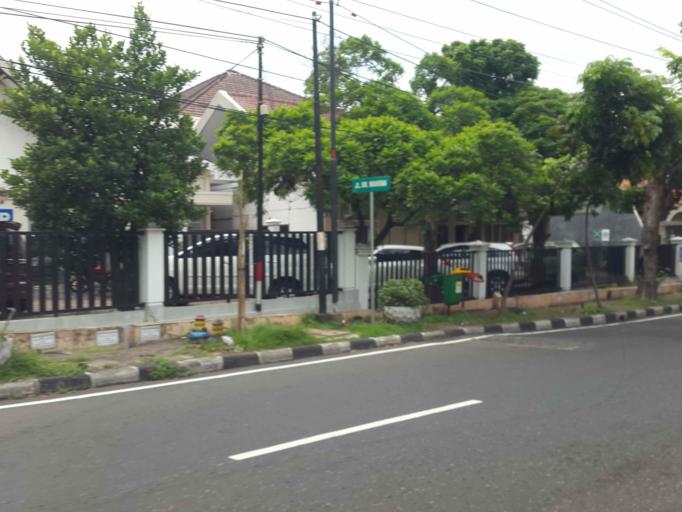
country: ID
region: Central Java
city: Semarang
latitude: -7.0164
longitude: 110.4288
